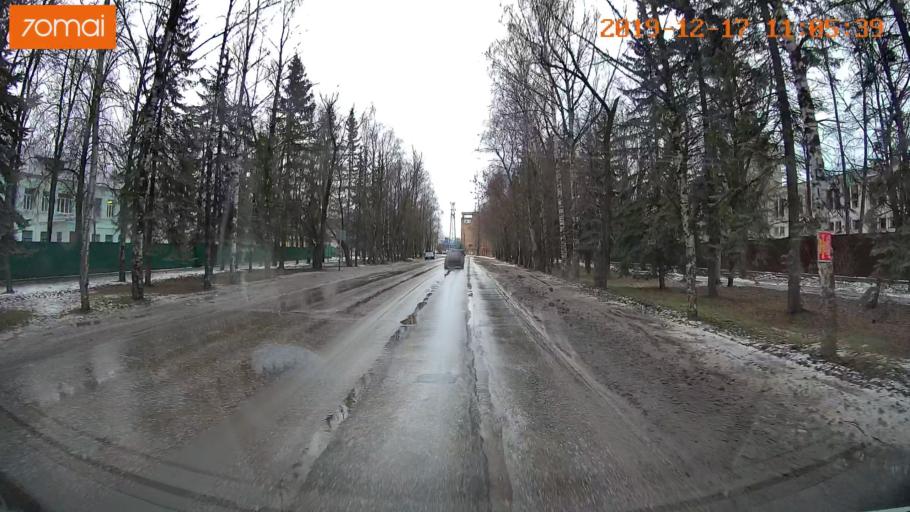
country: RU
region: Vladimir
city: Gus'-Khrustal'nyy
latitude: 55.6199
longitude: 40.6430
